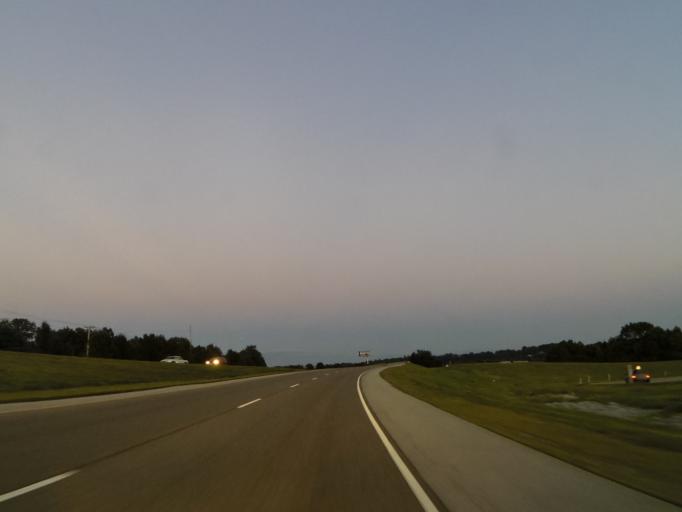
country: US
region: Tennessee
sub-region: Knox County
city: Farragut
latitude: 35.9142
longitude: -84.1204
